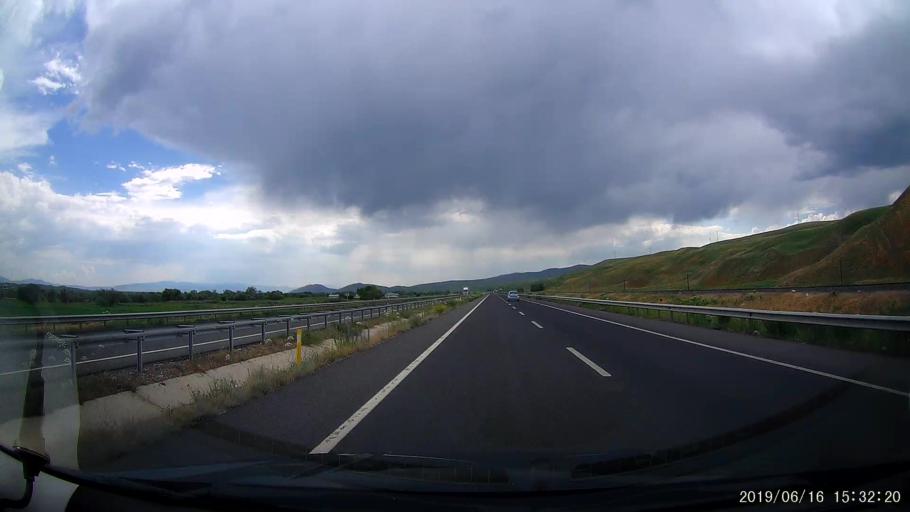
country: TR
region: Erzurum
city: Horasan
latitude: 40.0299
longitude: 42.0507
